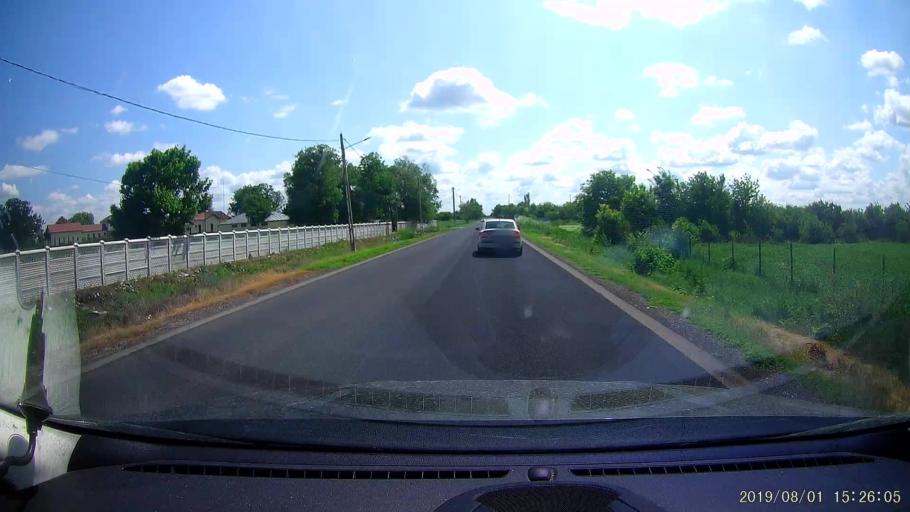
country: RO
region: Braila
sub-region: Comuna Viziru
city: Viziru
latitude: 45.0134
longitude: 27.7253
